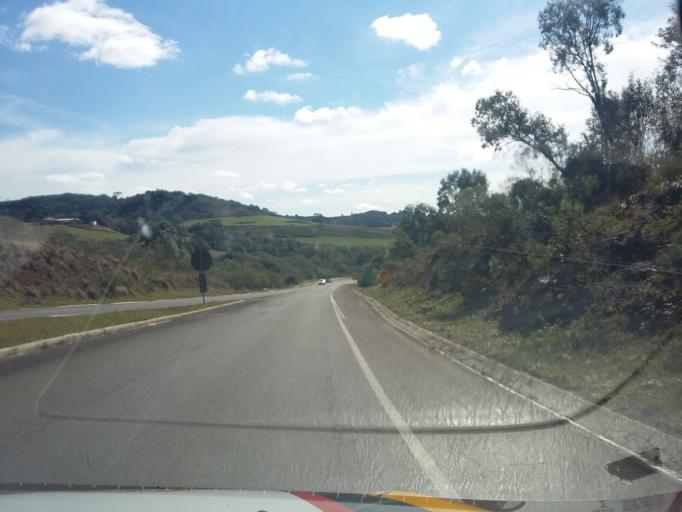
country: BR
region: Rio Grande do Sul
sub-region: Vacaria
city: Vacaria
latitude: -28.6211
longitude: -51.0426
